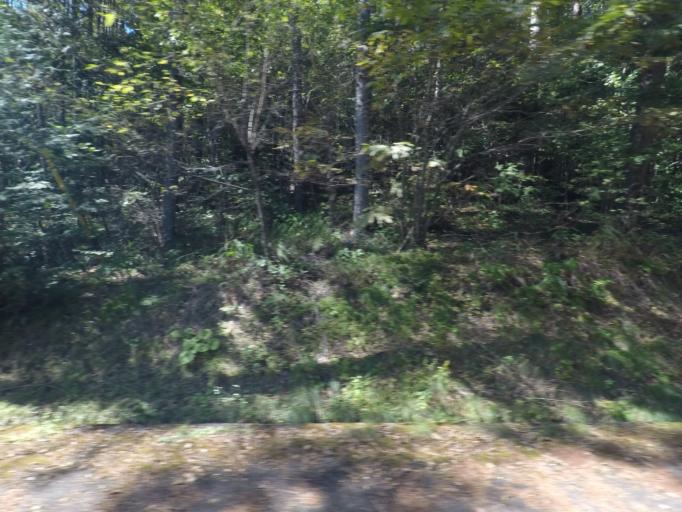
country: JP
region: Nagano
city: Shiojiri
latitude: 35.9979
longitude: 137.7339
